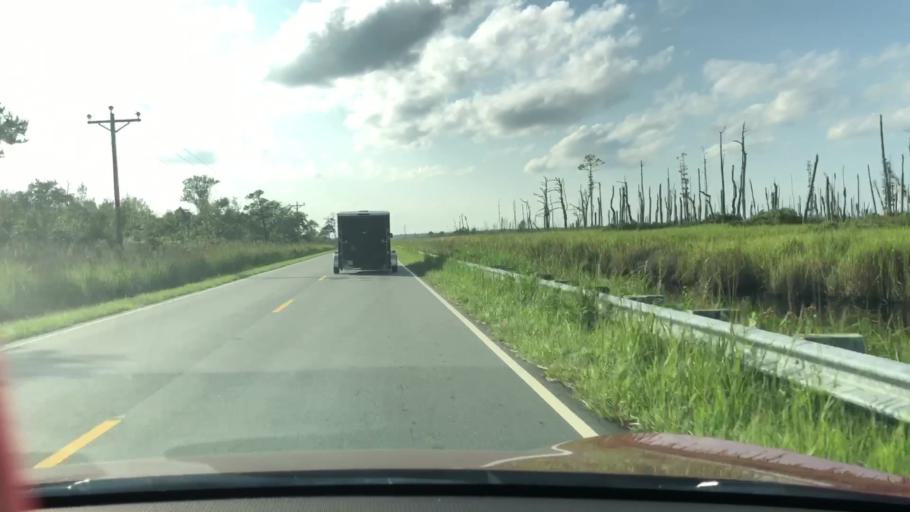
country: US
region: North Carolina
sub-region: Dare County
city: Wanchese
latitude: 35.6211
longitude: -75.8391
